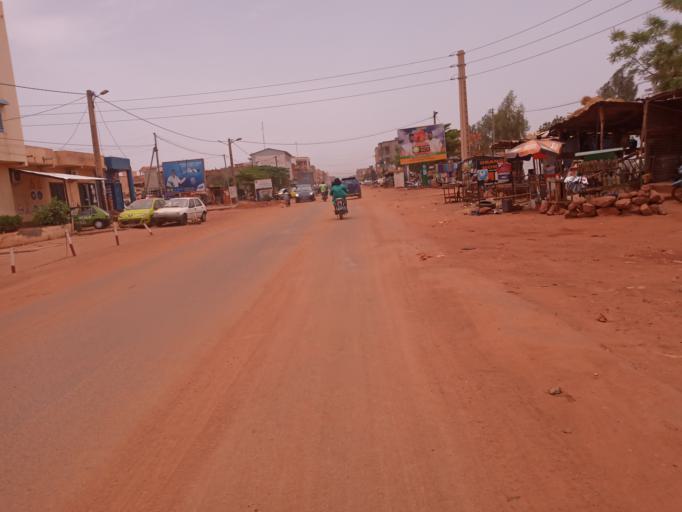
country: ML
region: Bamako
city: Bamako
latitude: 12.5820
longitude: -8.0207
